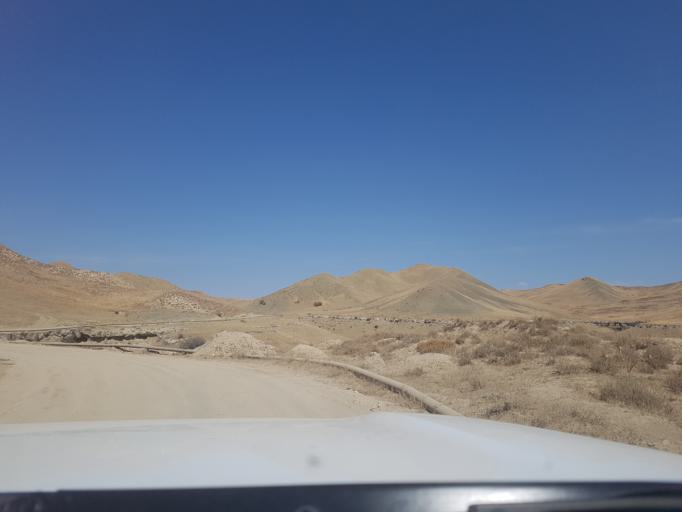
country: TM
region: Ahal
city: Baharly
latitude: 38.2525
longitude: 56.8910
